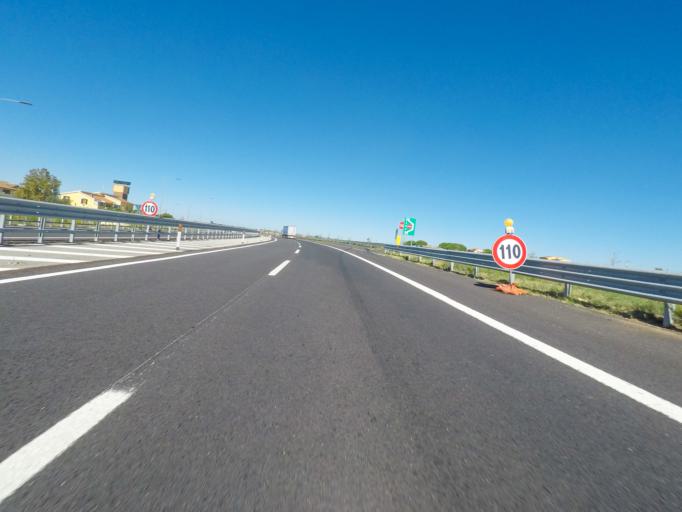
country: IT
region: Latium
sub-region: Citta metropolitana di Roma Capitale
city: Aurelia
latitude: 42.1820
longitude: 11.7892
